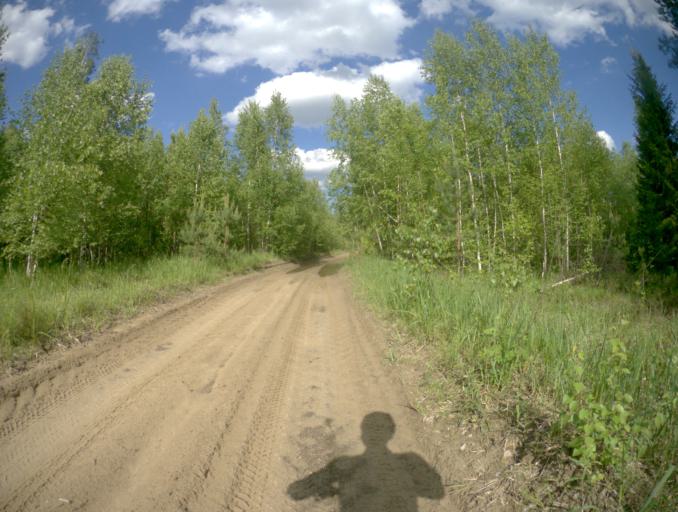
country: RU
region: Vladimir
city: Zolotkovo
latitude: 55.3297
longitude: 40.9706
